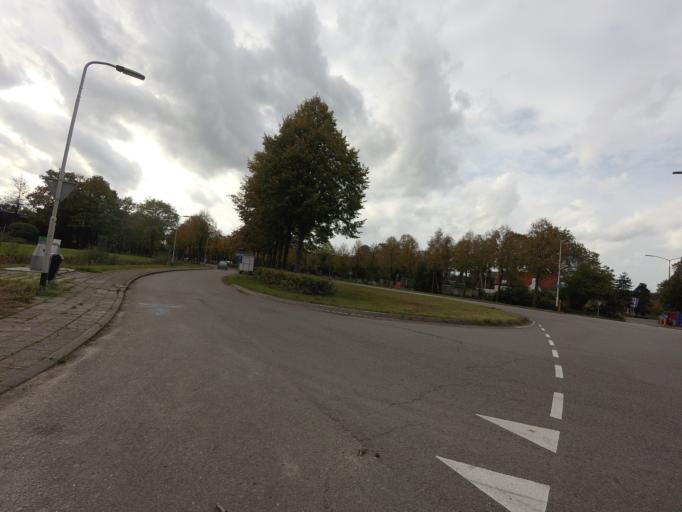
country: NL
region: North Brabant
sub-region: Gemeente Breda
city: Breda
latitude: 51.5655
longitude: 4.7469
